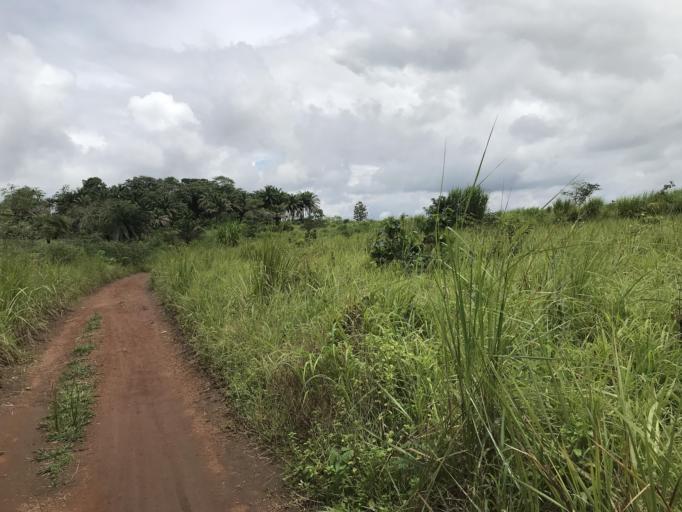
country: SL
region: Eastern Province
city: Buedu
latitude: 8.4710
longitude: -10.3219
